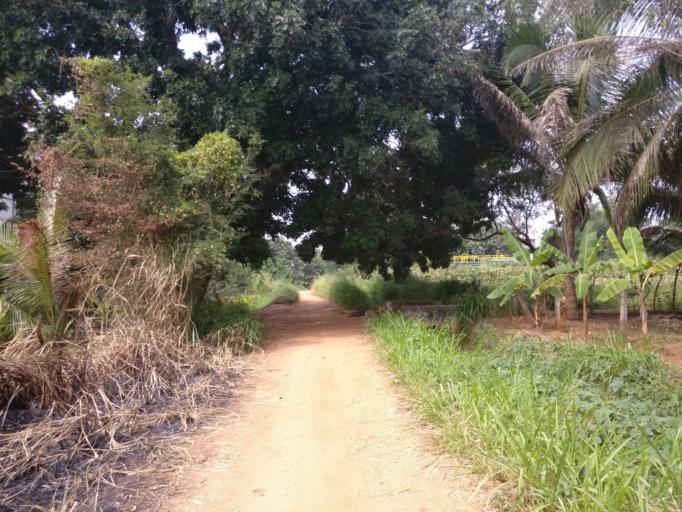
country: LK
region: Central
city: Dambulla
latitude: 7.8399
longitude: 80.6504
